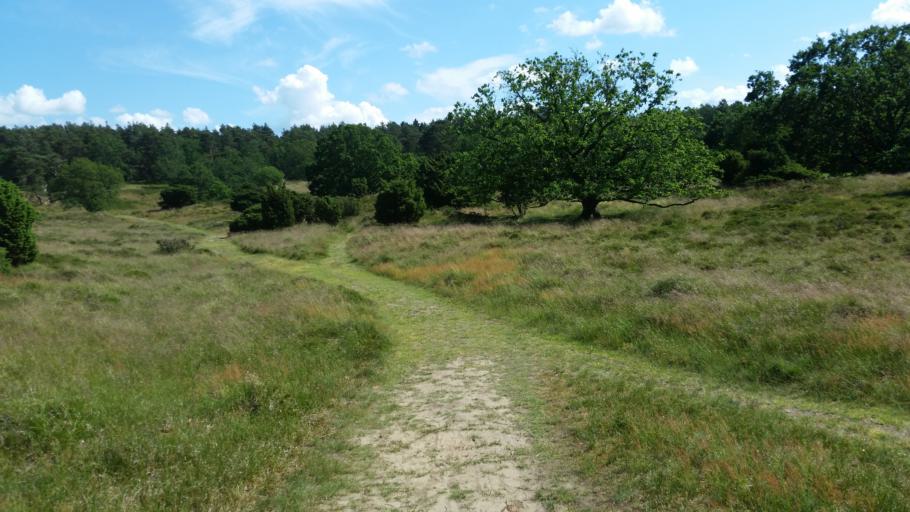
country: DK
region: Capital Region
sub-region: Helsingor Kommune
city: Hornbaek
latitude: 56.0851
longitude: 12.4034
